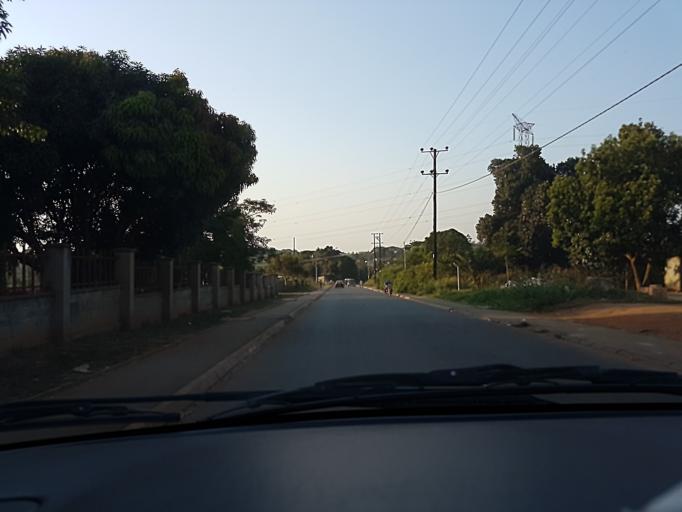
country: UG
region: Central Region
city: Kampala Central Division
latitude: 0.4010
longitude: 32.5903
